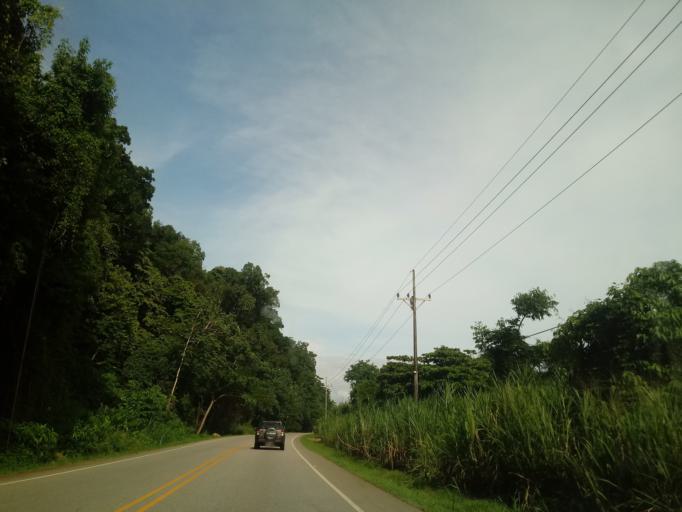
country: CR
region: San Jose
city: Daniel Flores
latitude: 9.1955
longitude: -83.7815
